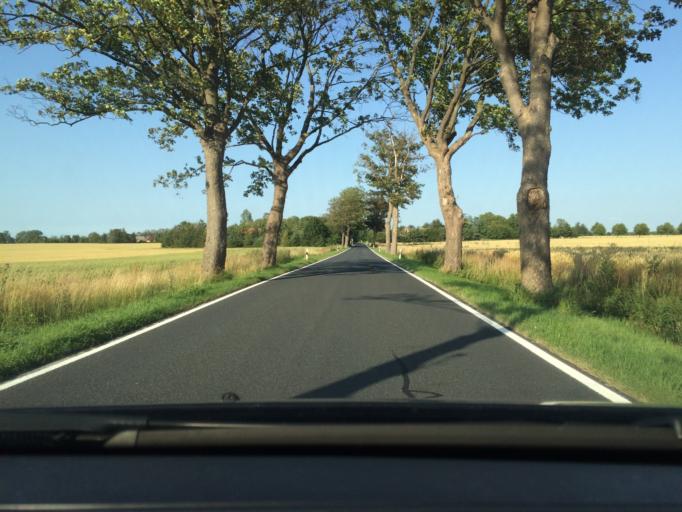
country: DE
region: Mecklenburg-Vorpommern
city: Niepars
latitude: 54.3178
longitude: 12.9292
